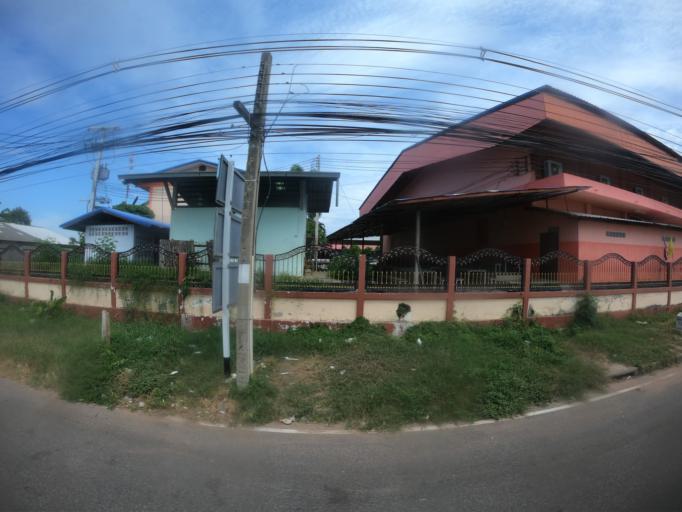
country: TH
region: Maha Sarakham
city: Chiang Yuen
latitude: 16.4115
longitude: 103.0941
